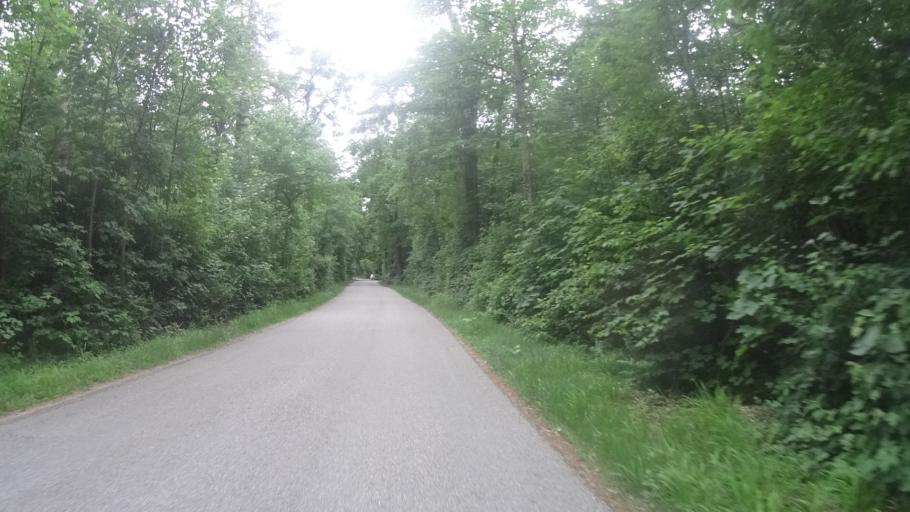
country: DE
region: Bavaria
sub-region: Upper Bavaria
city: Oberschleissheim
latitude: 48.2574
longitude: 11.5664
